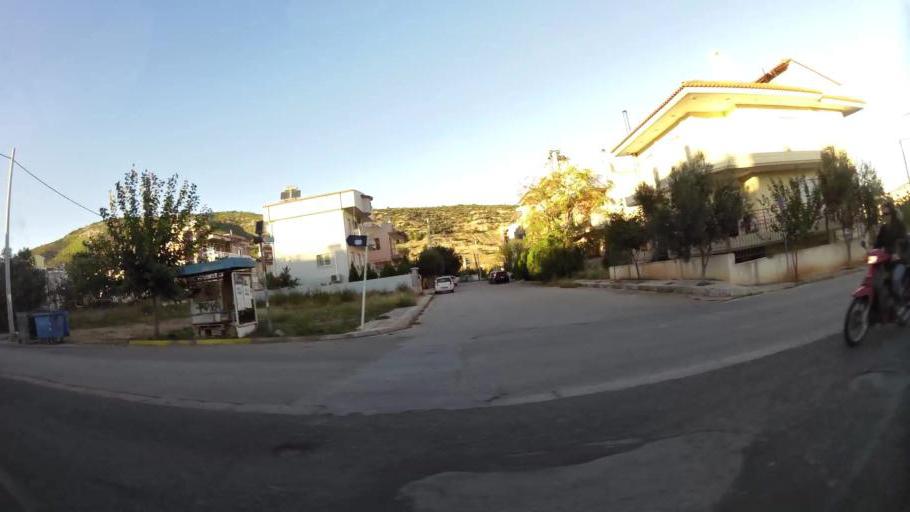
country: GR
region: Attica
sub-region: Nomarchia Dytikis Attikis
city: Ano Liosia
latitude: 38.0922
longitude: 23.7043
